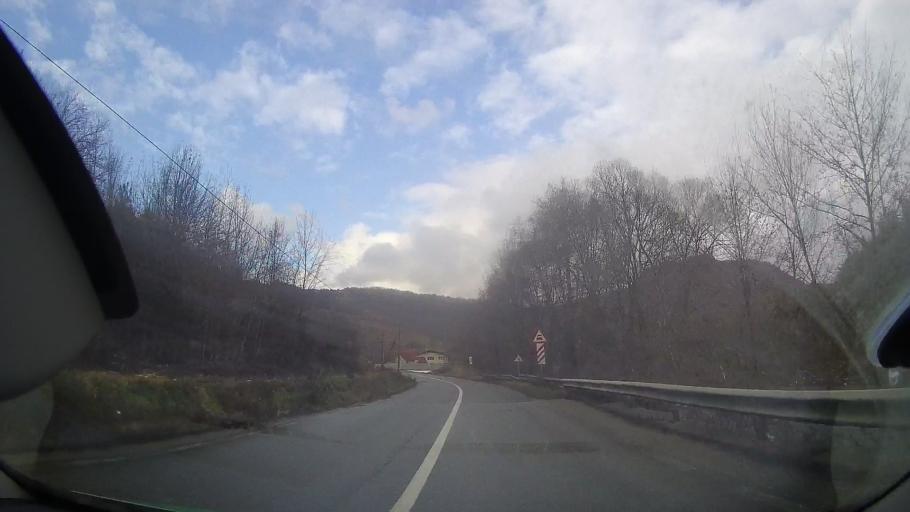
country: RO
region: Alba
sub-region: Comuna Ocolis
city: Ocolis
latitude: 46.4332
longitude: 23.4588
